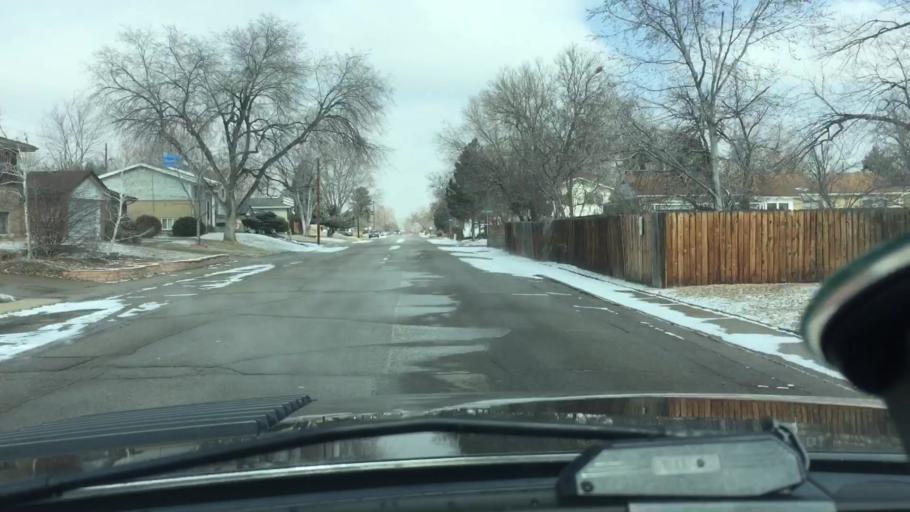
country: US
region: Colorado
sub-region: Adams County
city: Northglenn
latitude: 39.8795
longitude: -105.0056
